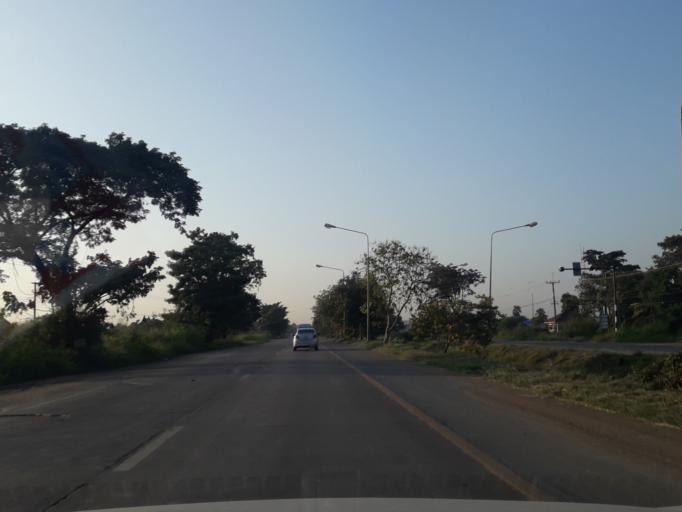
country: TH
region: Phra Nakhon Si Ayutthaya
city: Bang Pa-in
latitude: 14.2442
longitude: 100.5373
